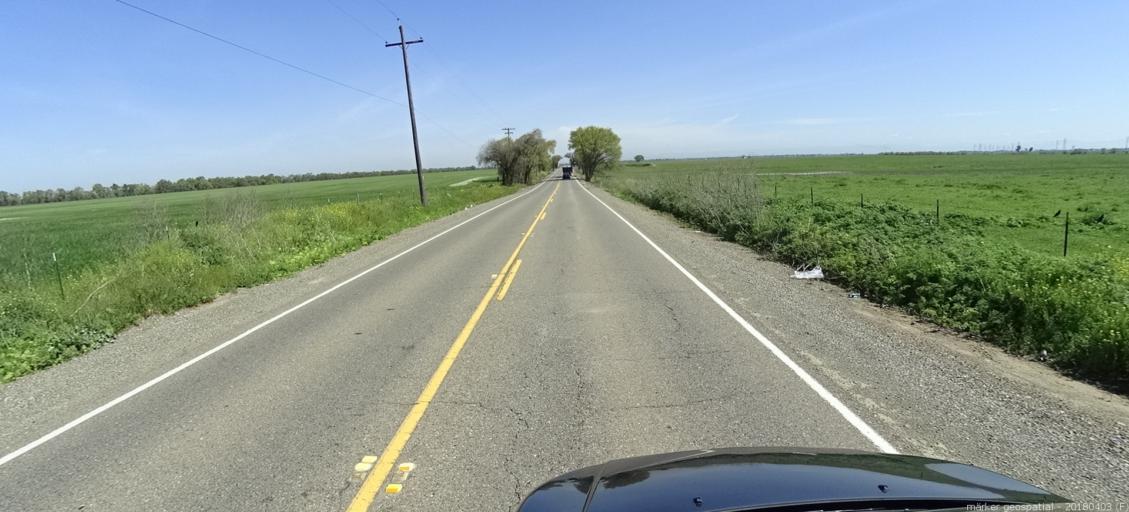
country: US
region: California
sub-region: Sacramento County
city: Elk Grove
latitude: 38.3493
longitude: -121.3274
